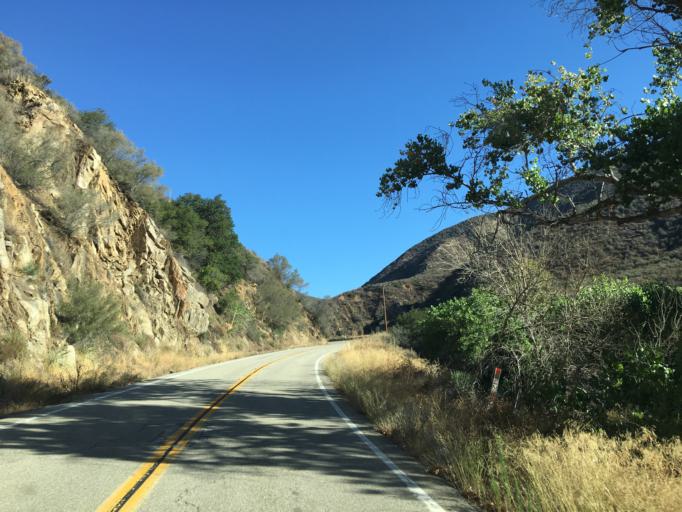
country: US
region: California
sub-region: Los Angeles County
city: Castaic
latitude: 34.5813
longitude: -118.5576
